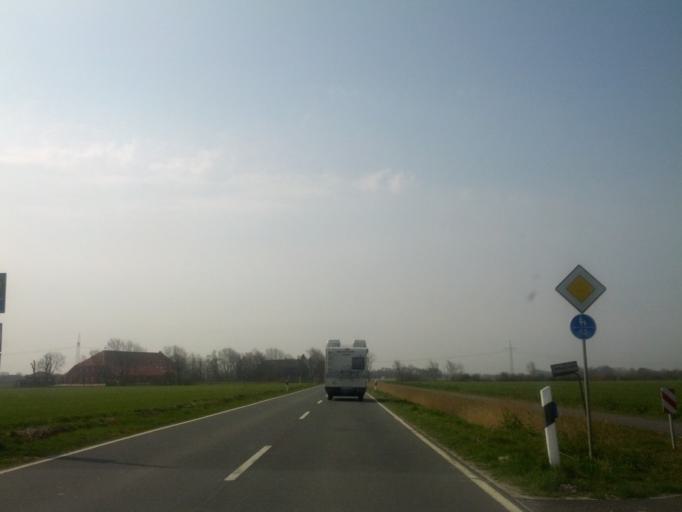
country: DE
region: Lower Saxony
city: Norden
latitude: 53.6202
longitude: 7.1911
